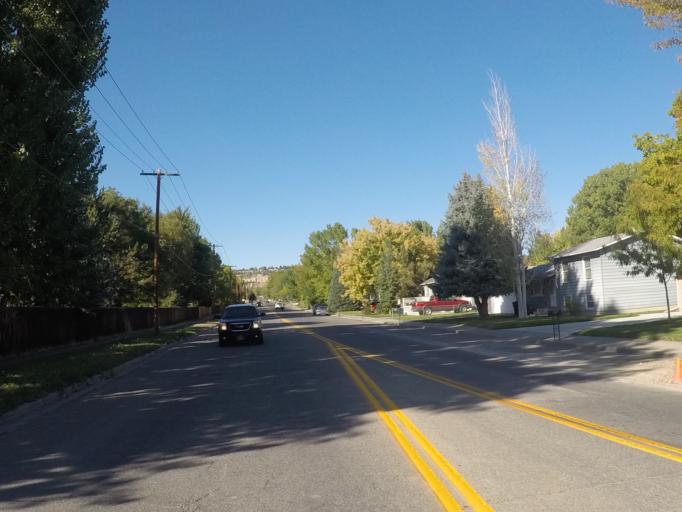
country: US
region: Montana
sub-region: Yellowstone County
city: Billings
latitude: 45.7859
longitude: -108.5903
